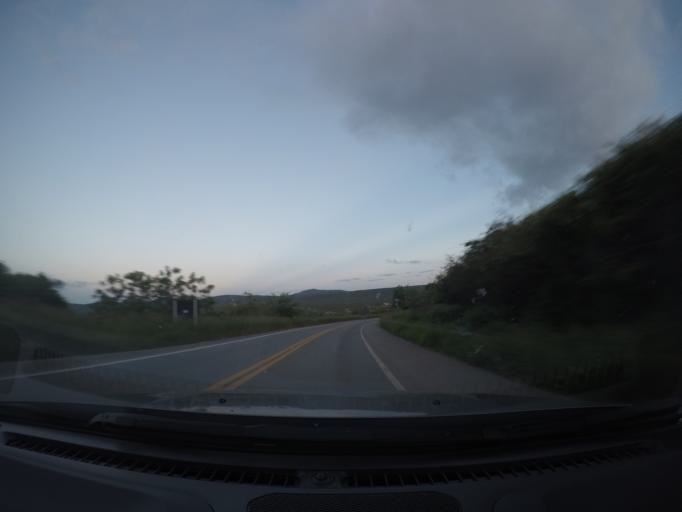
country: BR
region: Bahia
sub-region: Seabra
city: Seabra
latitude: -12.4265
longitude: -41.7638
